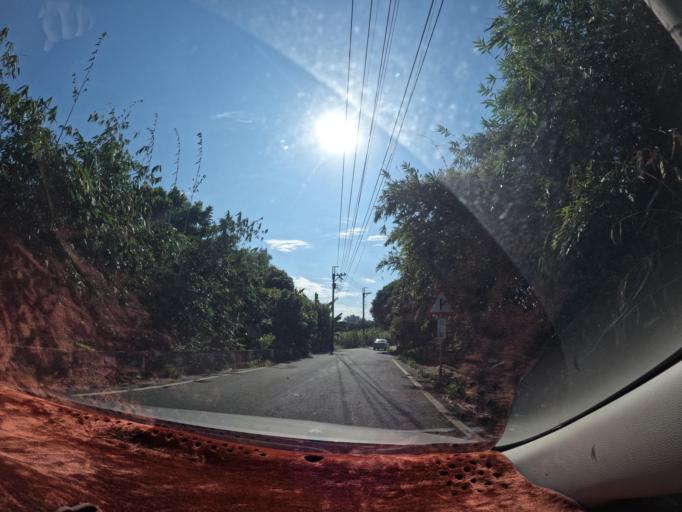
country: TW
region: Taiwan
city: Yujing
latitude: 23.0491
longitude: 120.4016
